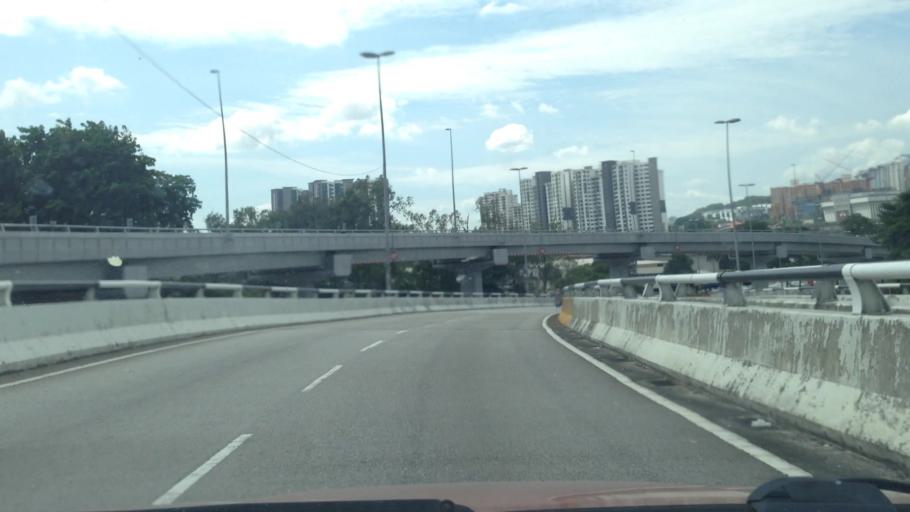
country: MY
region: Kuala Lumpur
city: Kuala Lumpur
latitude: 3.0919
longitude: 101.6902
